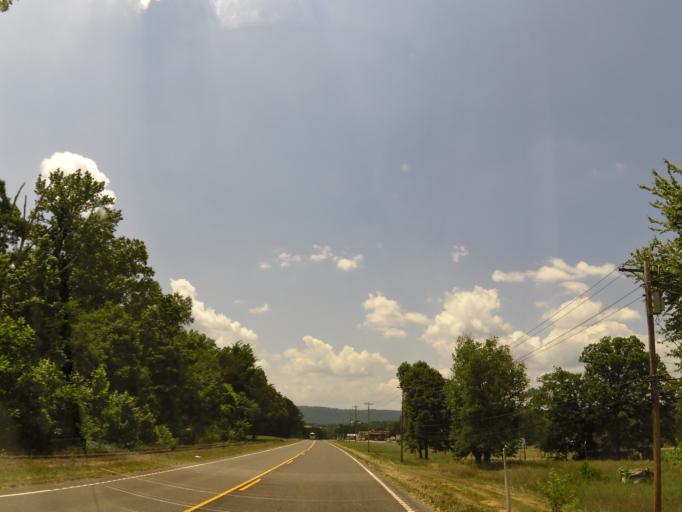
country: US
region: Tennessee
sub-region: Rhea County
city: Spring City
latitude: 35.6444
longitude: -84.8493
